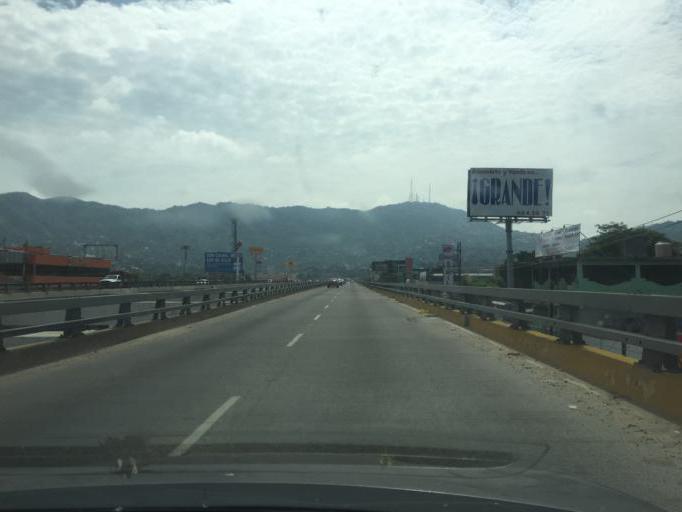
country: MX
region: Guerrero
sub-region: Acapulco de Juarez
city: Nueva Frontera
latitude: 16.8952
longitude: -99.8329
